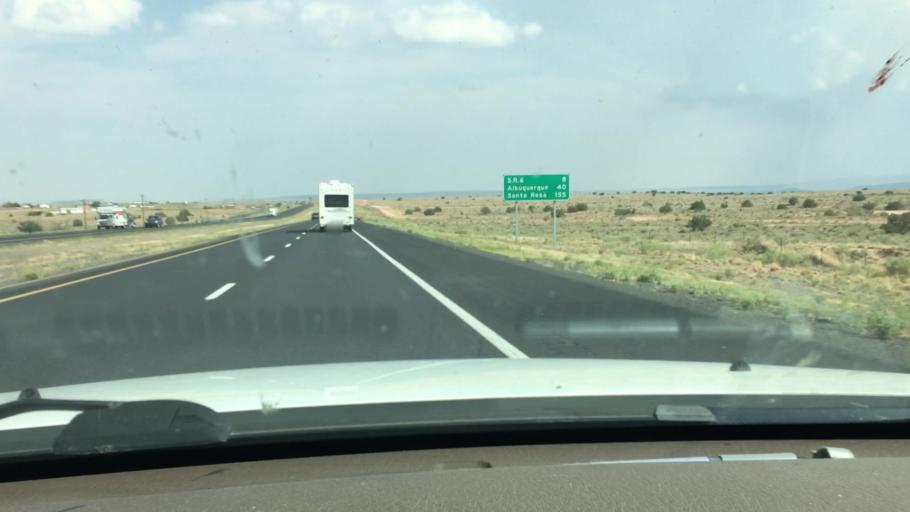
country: US
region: New Mexico
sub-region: Cibola County
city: Laguna
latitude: 35.0054
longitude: -107.3144
